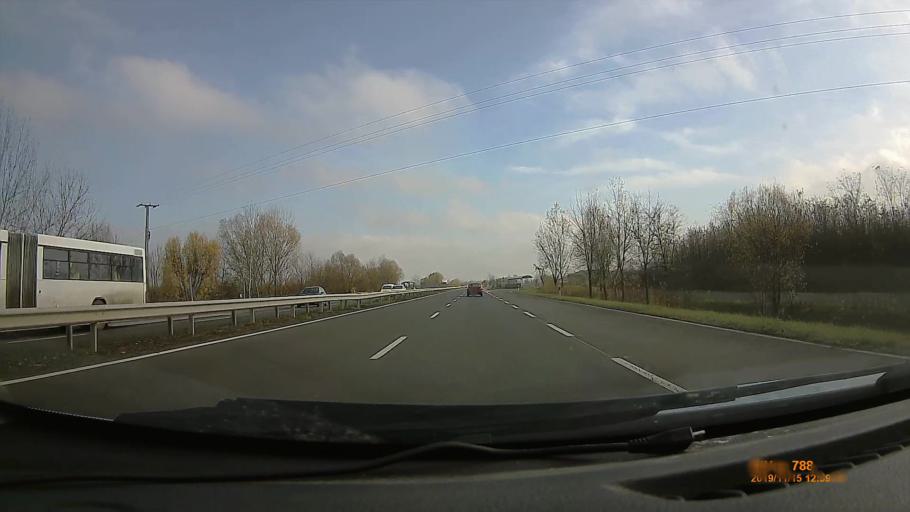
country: HU
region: Bekes
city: Doboz
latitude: 46.6676
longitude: 21.1906
